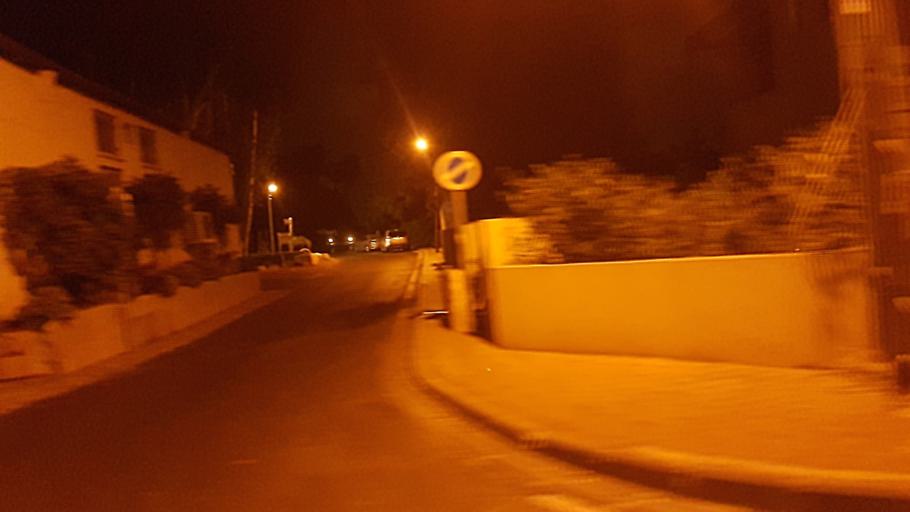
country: IL
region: Central District
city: Hod HaSharon
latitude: 32.1665
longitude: 34.8866
